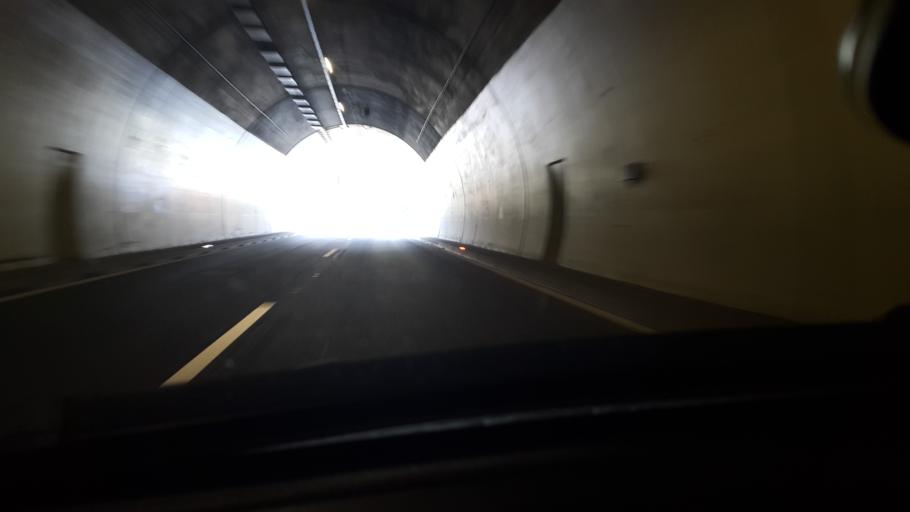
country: AT
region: Carinthia
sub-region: Politischer Bezirk Volkermarkt
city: Griffen
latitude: 46.7090
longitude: 14.7786
